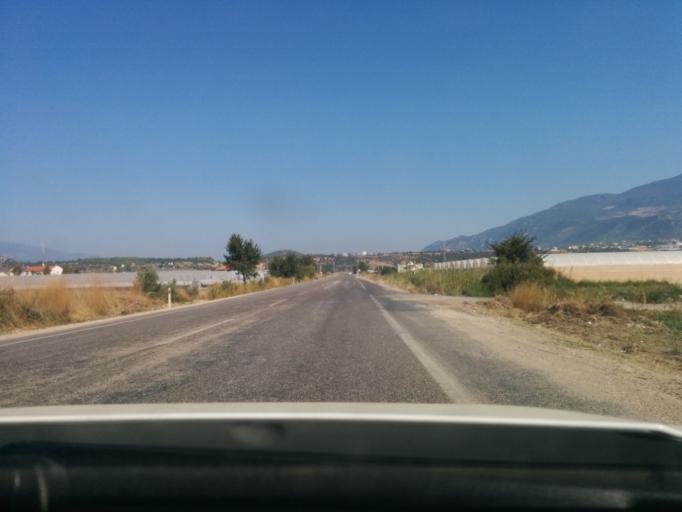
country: TR
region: Antalya
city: Kalkan
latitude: 36.3369
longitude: 29.3344
